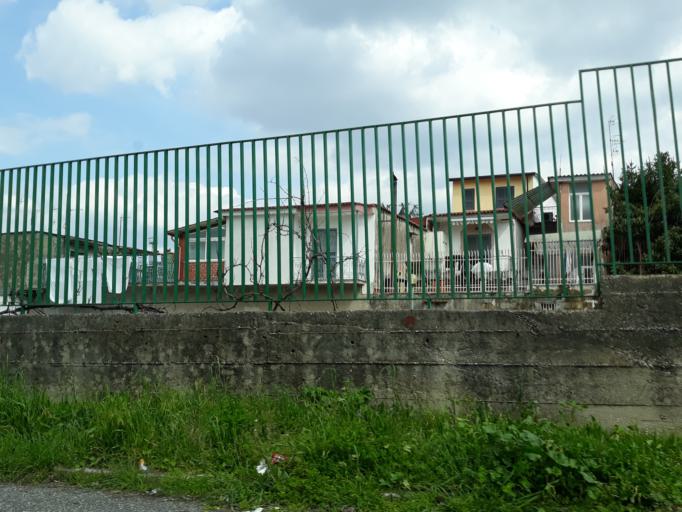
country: IT
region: Campania
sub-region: Provincia di Napoli
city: Mugnano di Napoli
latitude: 40.8884
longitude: 14.2328
